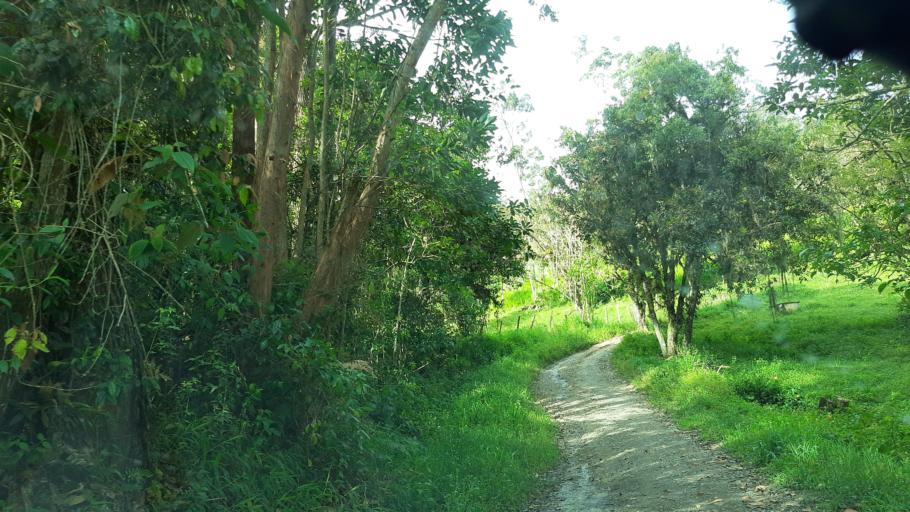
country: CO
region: Boyaca
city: Garagoa
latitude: 5.0377
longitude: -73.3486
